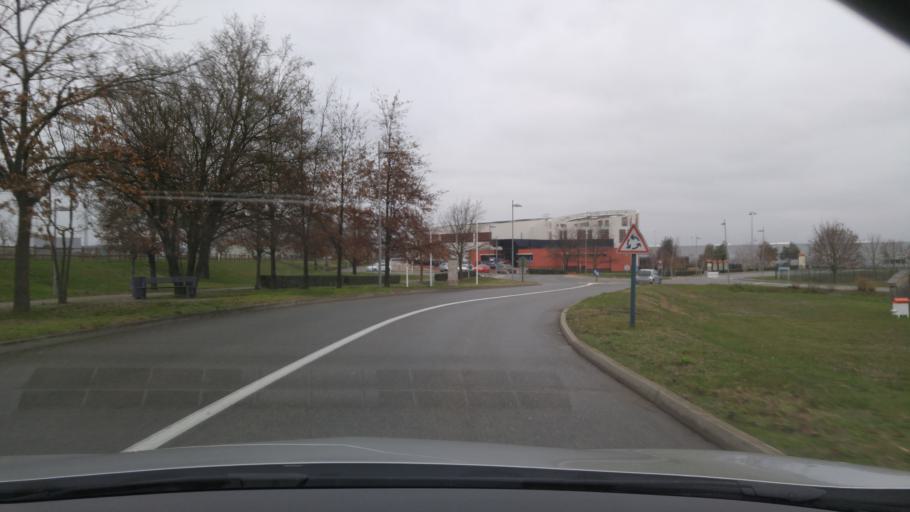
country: FR
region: Rhone-Alpes
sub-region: Departement de l'Isere
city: Saint-Quentin-Fallavier
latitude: 45.6383
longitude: 5.1081
